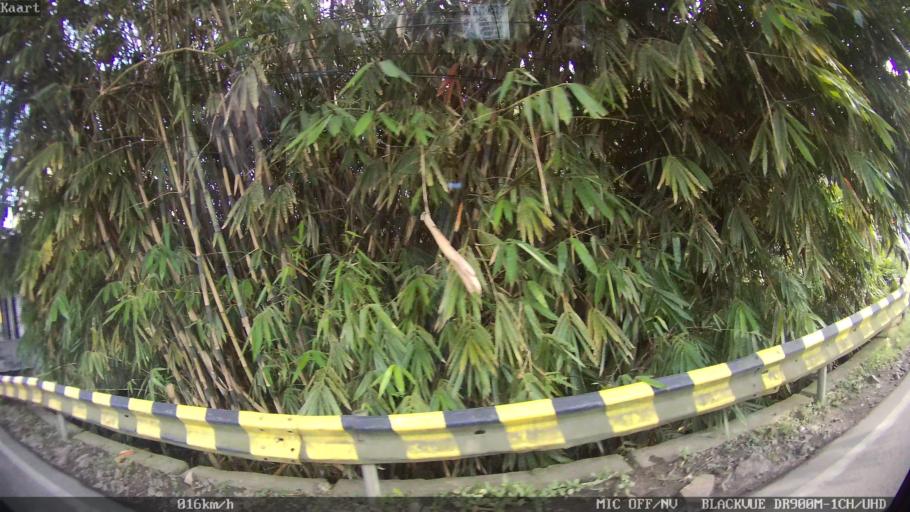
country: ID
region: Lampung
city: Kedaton
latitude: -5.3863
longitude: 105.2673
